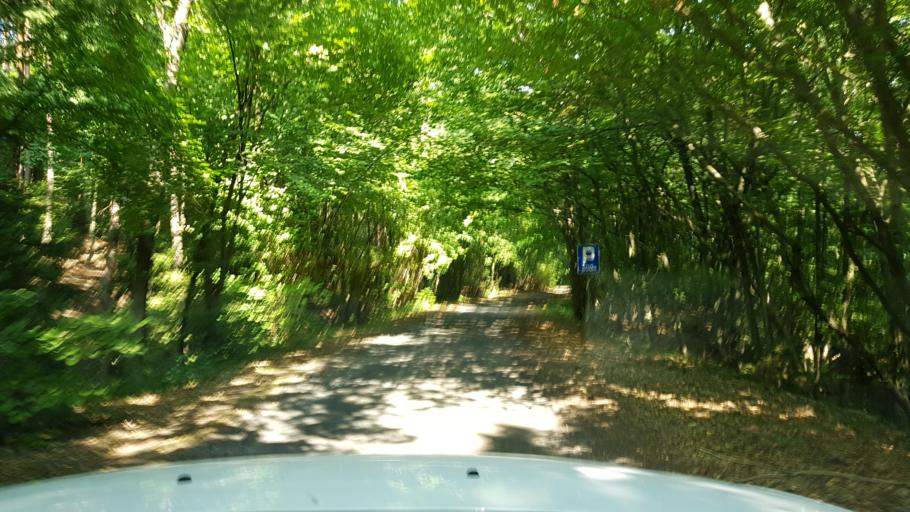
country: DE
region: Brandenburg
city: Neulewin
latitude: 52.8070
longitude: 14.3165
